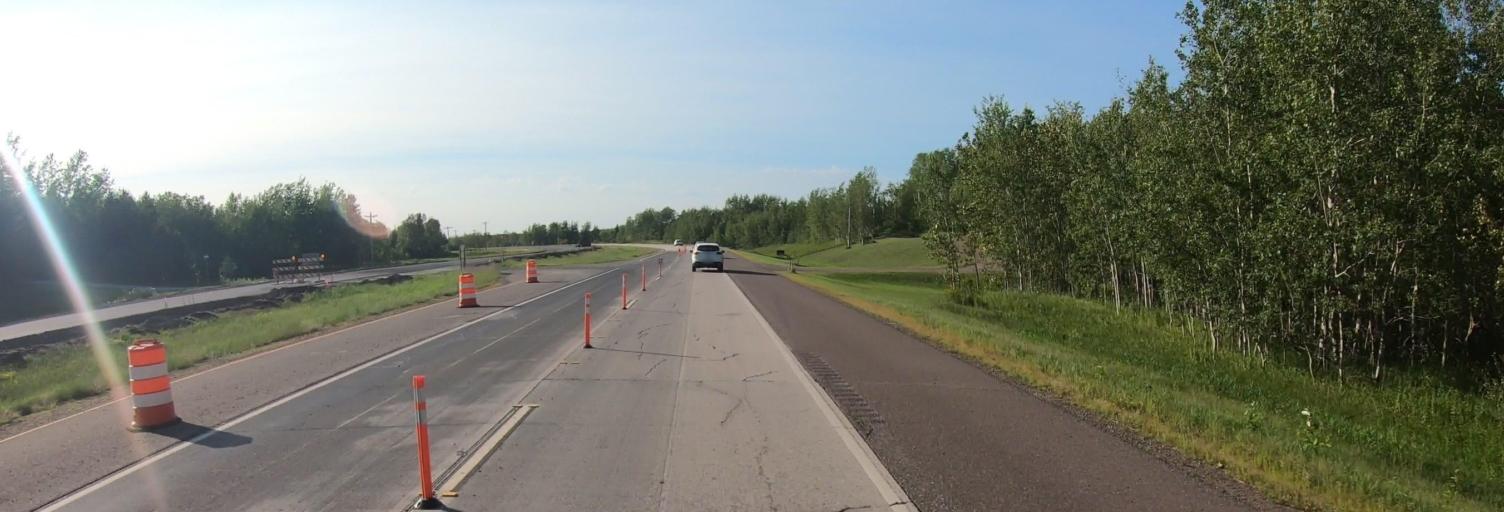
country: US
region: Minnesota
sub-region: Saint Louis County
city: Hermantown
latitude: 46.9187
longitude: -92.4002
